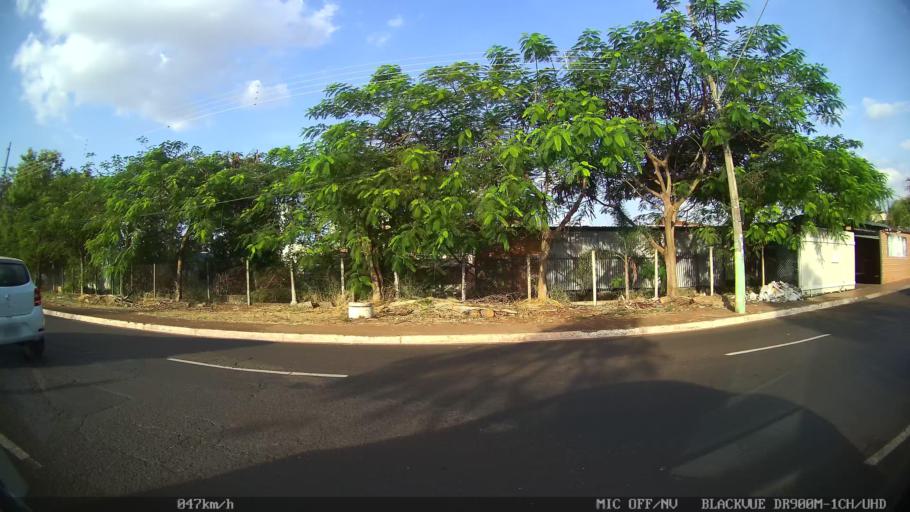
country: BR
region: Sao Paulo
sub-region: Ribeirao Preto
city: Ribeirao Preto
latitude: -21.1635
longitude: -47.8168
